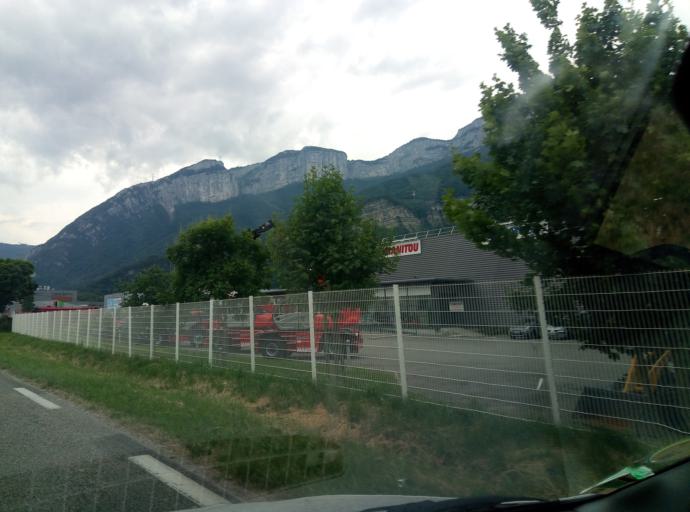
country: FR
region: Rhone-Alpes
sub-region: Departement de l'Isere
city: Noyarey
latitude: 45.2575
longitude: 5.6273
